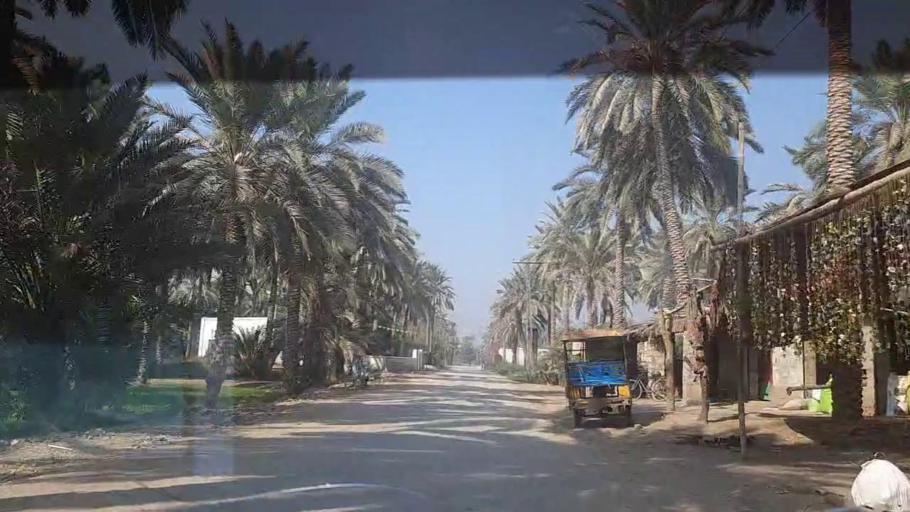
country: PK
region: Sindh
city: Kot Diji
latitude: 27.3790
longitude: 68.6911
